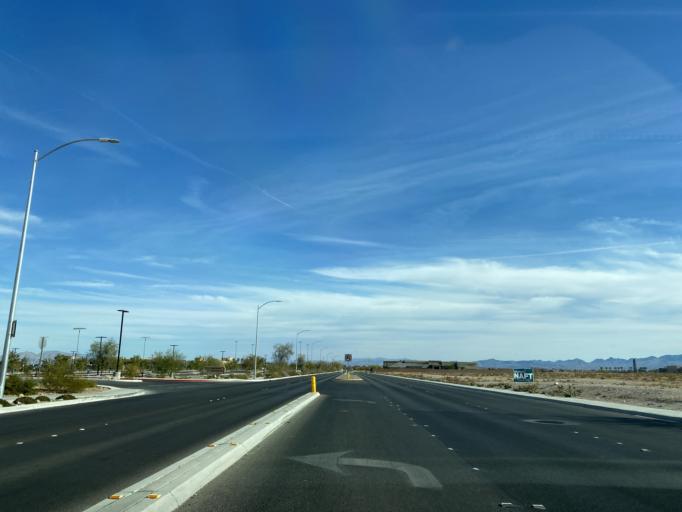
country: US
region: Nevada
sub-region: Clark County
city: Enterprise
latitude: 36.0482
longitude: -115.2750
